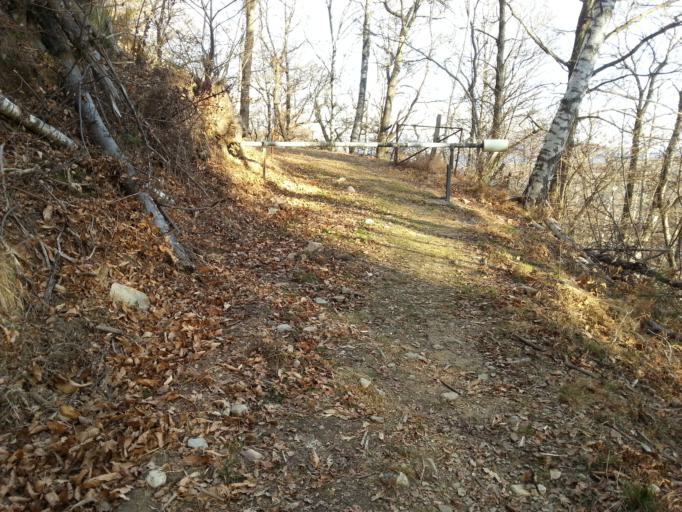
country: CH
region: Ticino
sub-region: Lugano District
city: Gravesano
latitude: 46.0415
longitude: 8.8707
